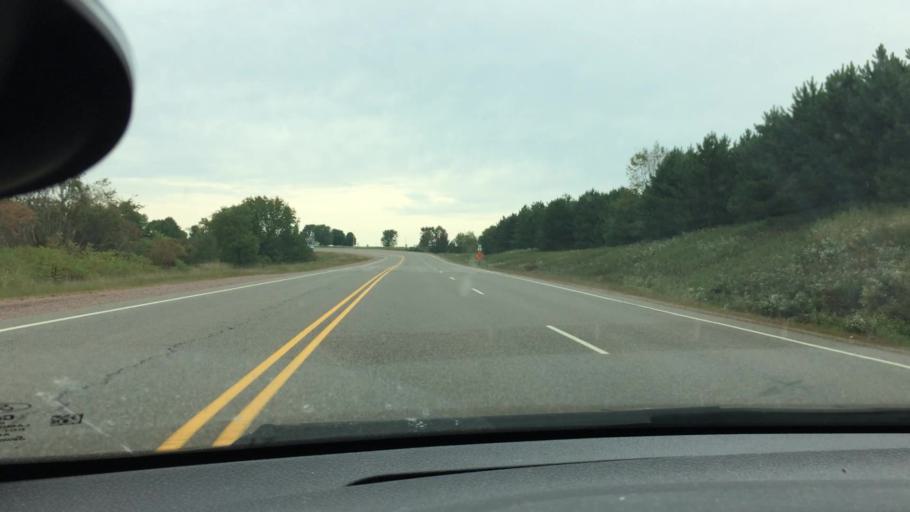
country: US
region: Wisconsin
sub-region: Clark County
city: Neillsville
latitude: 44.5575
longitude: -90.6407
